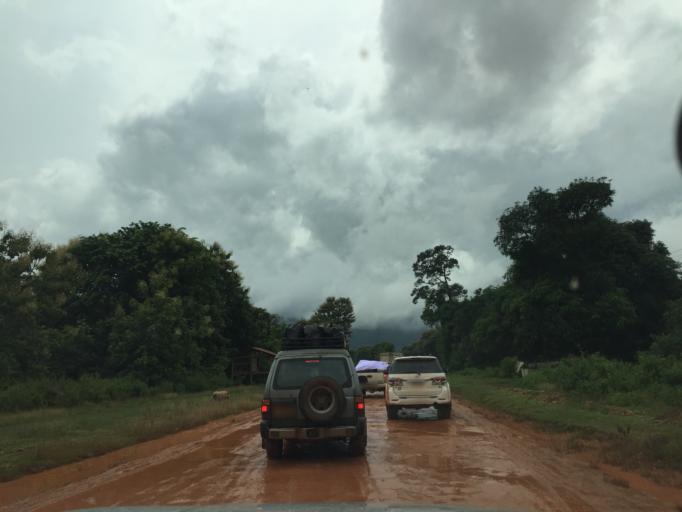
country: LA
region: Attapu
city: Attapu
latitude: 14.8077
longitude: 106.7678
